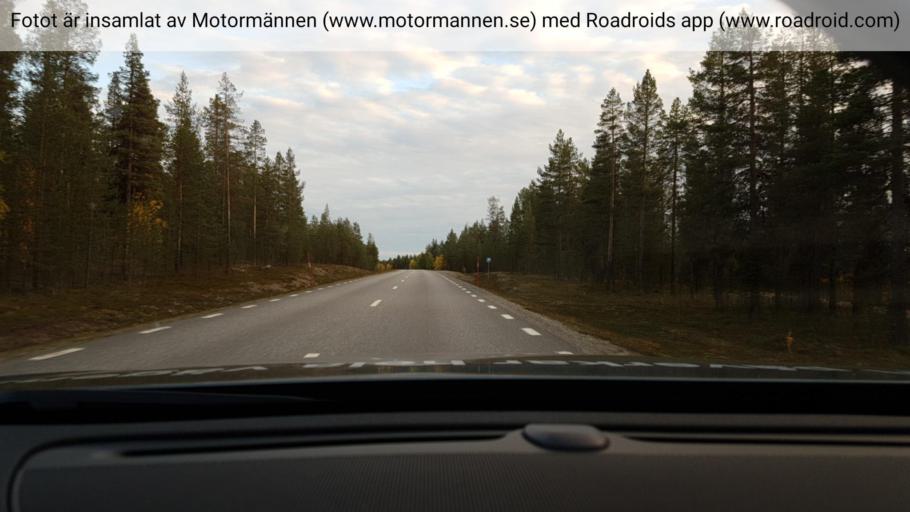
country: SE
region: Norrbotten
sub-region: Jokkmokks Kommun
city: Jokkmokk
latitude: 66.3977
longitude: 19.6962
